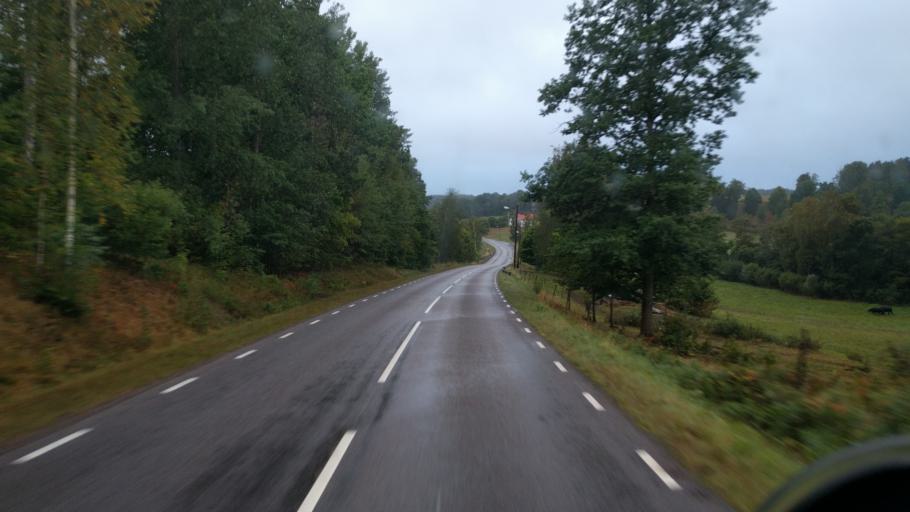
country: SE
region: Kalmar
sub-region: Vasterviks Kommun
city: Ankarsrum
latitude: 57.8372
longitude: 16.2574
